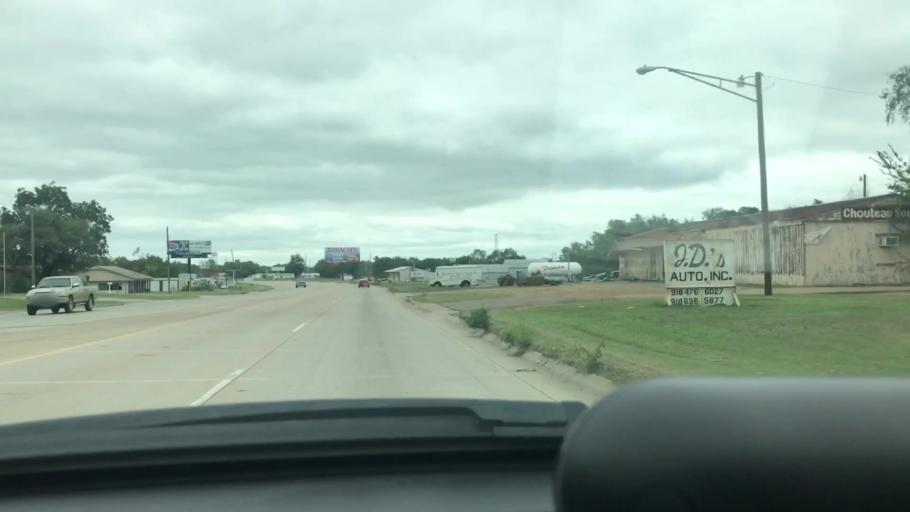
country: US
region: Oklahoma
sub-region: Mayes County
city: Chouteau
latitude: 36.1735
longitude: -95.3419
